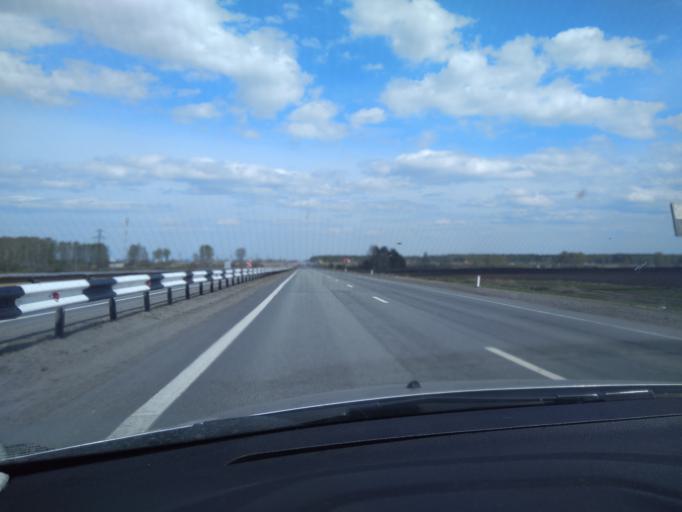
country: RU
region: Sverdlovsk
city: Zavodouspenskoye
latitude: 57.0925
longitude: 65.1184
